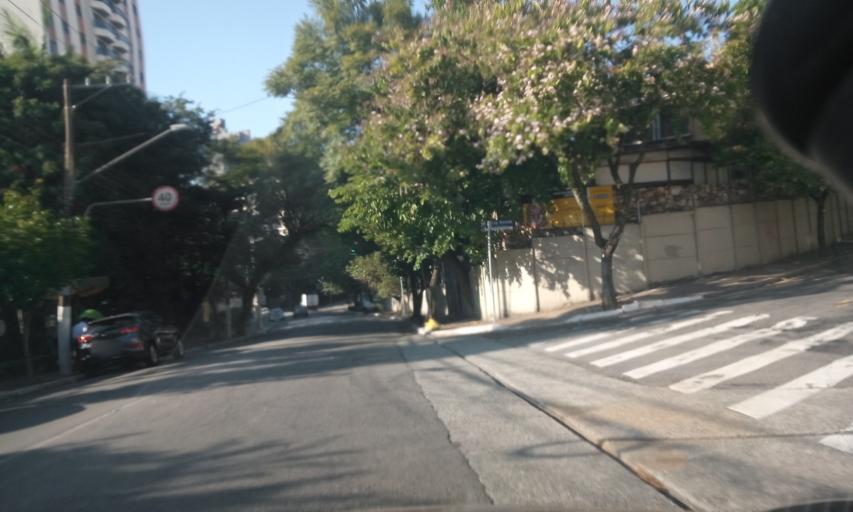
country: BR
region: Sao Paulo
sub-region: Sao Paulo
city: Sao Paulo
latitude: -23.5942
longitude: -46.6329
